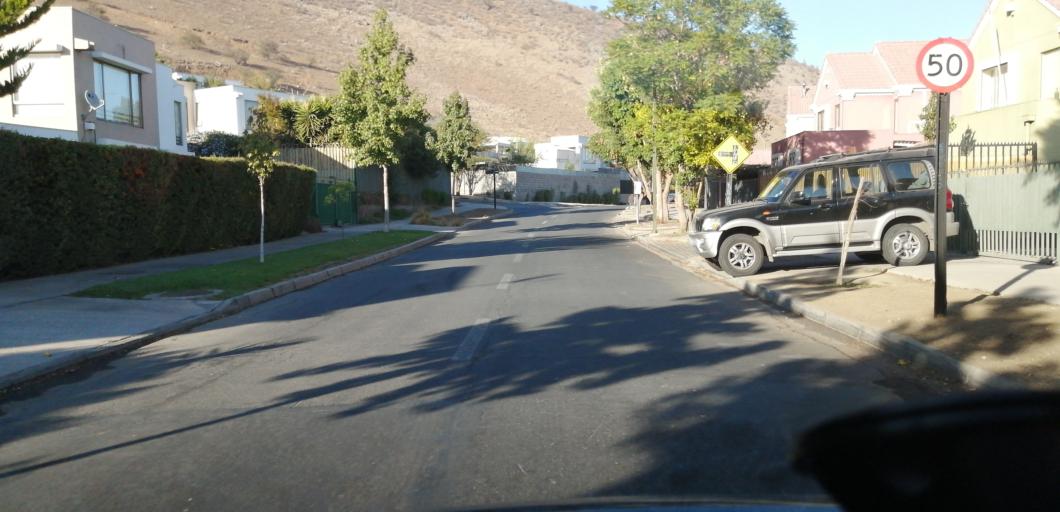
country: CL
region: Santiago Metropolitan
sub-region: Provincia de Santiago
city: Lo Prado
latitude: -33.4506
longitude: -70.8388
